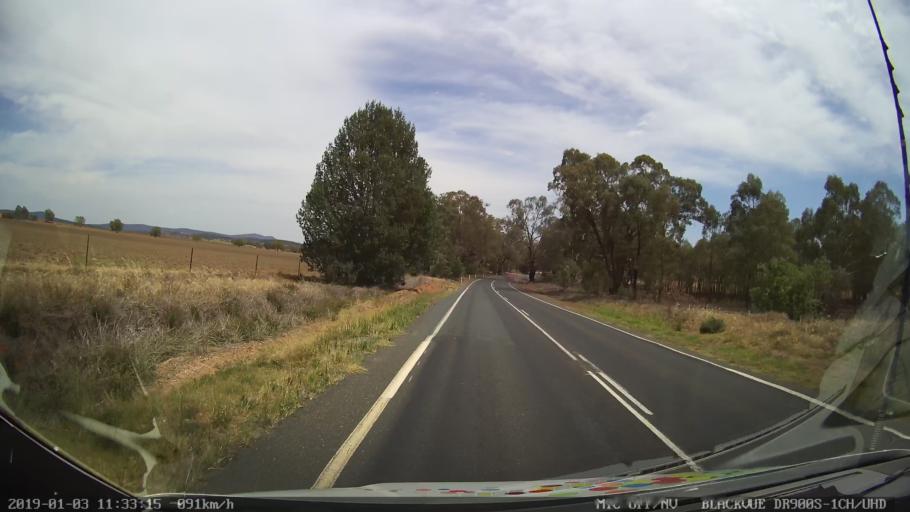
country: AU
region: New South Wales
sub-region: Weddin
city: Grenfell
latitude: -33.9489
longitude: 148.1725
